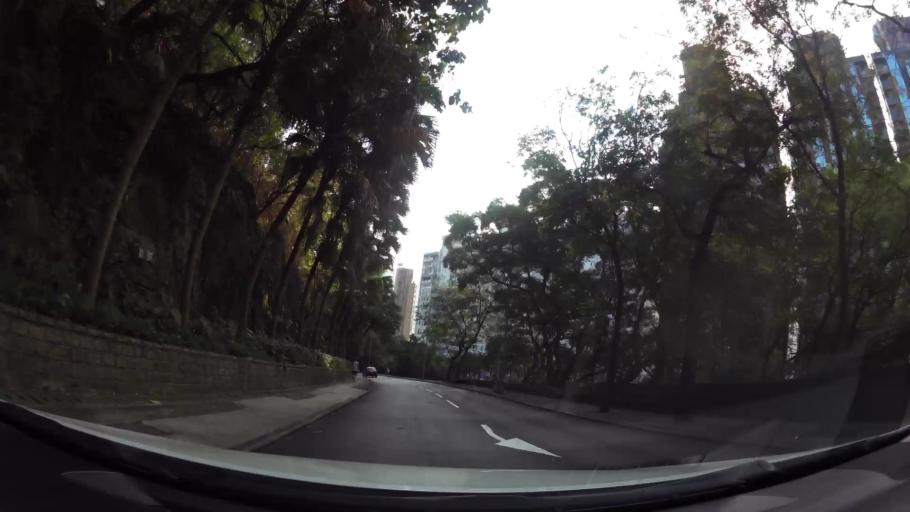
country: HK
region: Wanchai
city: Wan Chai
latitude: 22.2820
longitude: 114.1943
